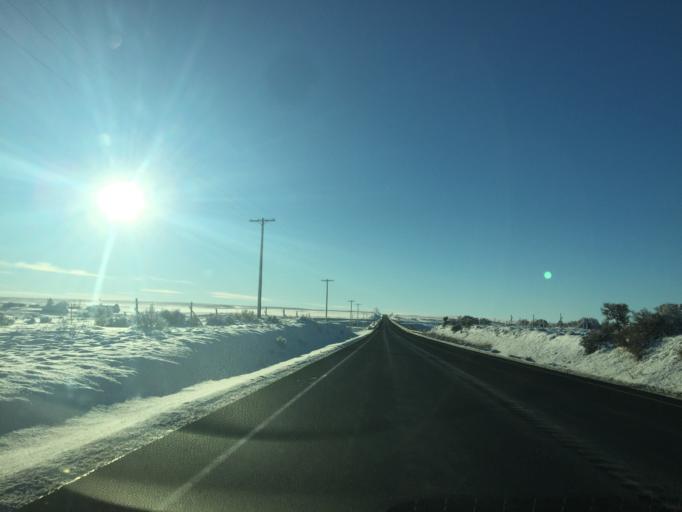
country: US
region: Washington
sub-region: Okanogan County
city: Coulee Dam
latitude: 47.7411
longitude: -118.8378
